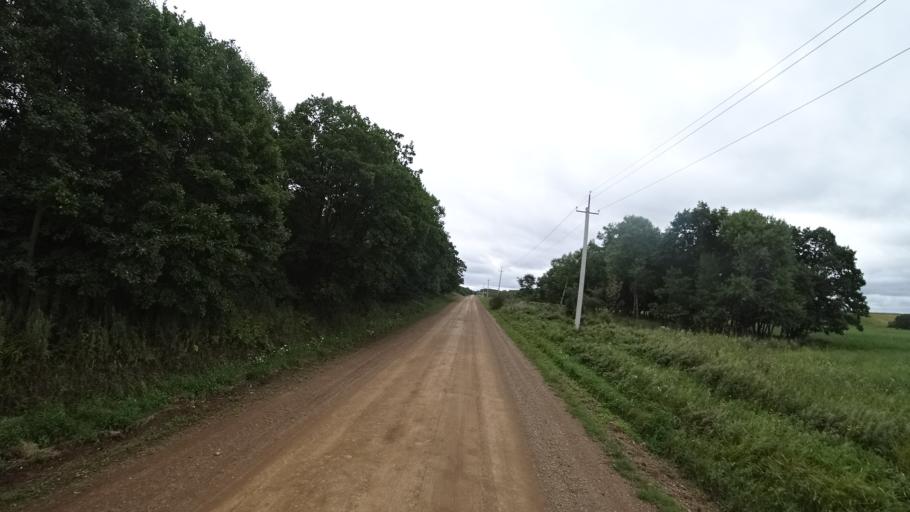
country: RU
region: Primorskiy
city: Chernigovka
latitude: 44.4687
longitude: 132.5844
